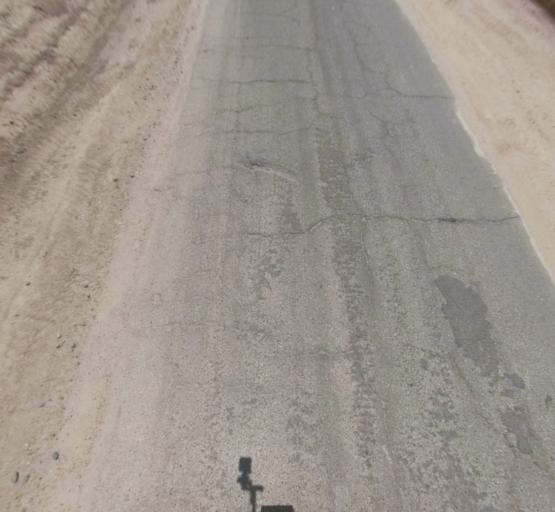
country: US
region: California
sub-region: Fresno County
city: Biola
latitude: 36.8189
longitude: -120.1149
